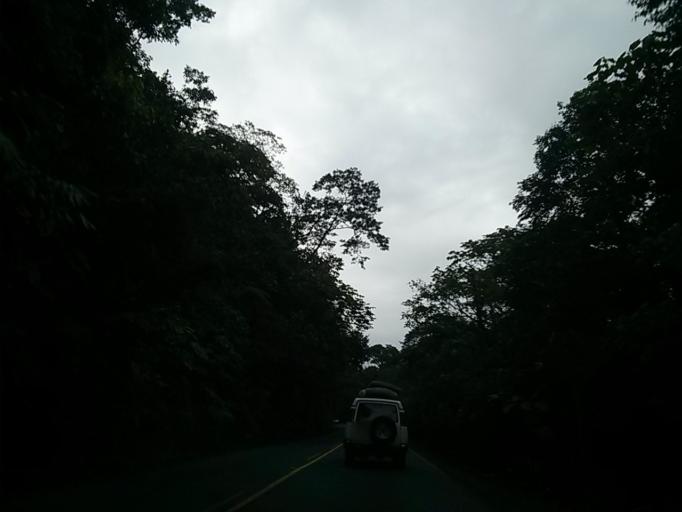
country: CR
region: San Jose
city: Dulce Nombre de Jesus
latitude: 10.1268
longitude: -83.9674
